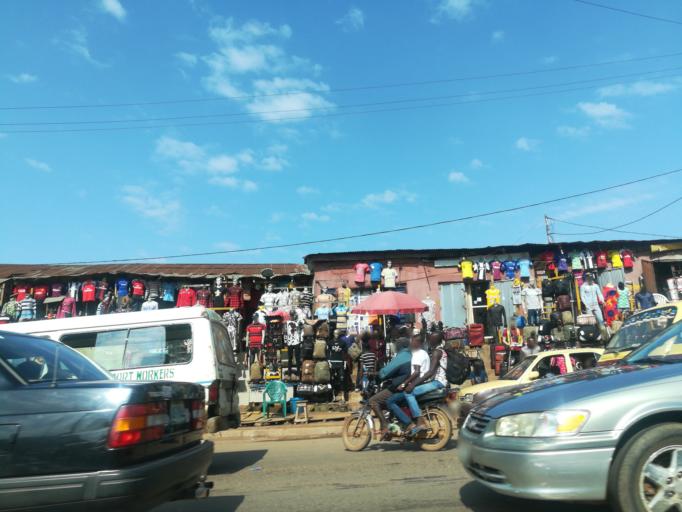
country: NG
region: Oyo
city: Ibadan
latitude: 7.4044
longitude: 3.9444
